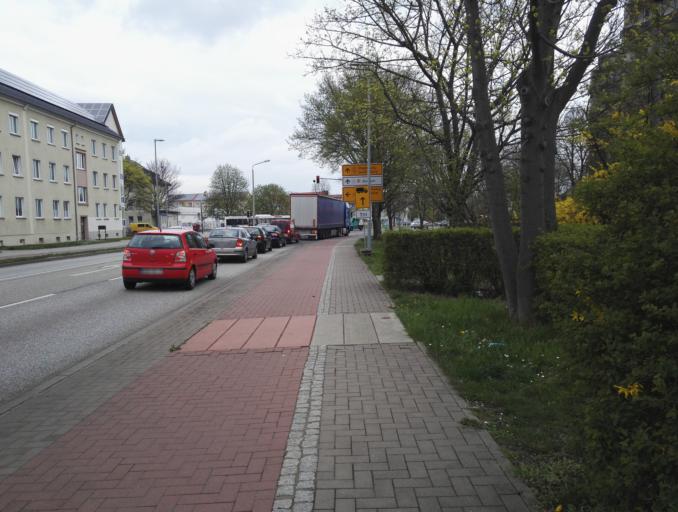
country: DE
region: Saxony-Anhalt
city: Halberstadt
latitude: 51.8921
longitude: 11.0572
